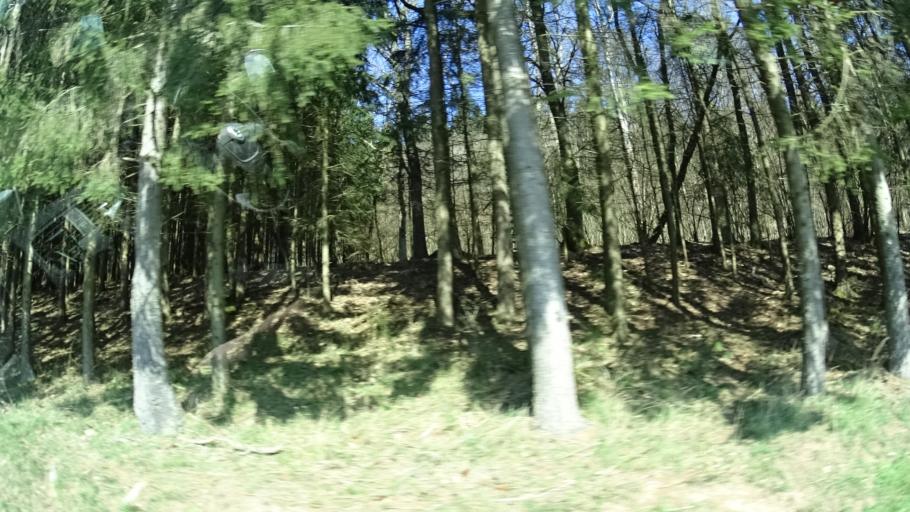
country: DE
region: Rheinland-Pfalz
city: Niederhambach
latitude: 49.6845
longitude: 7.1854
